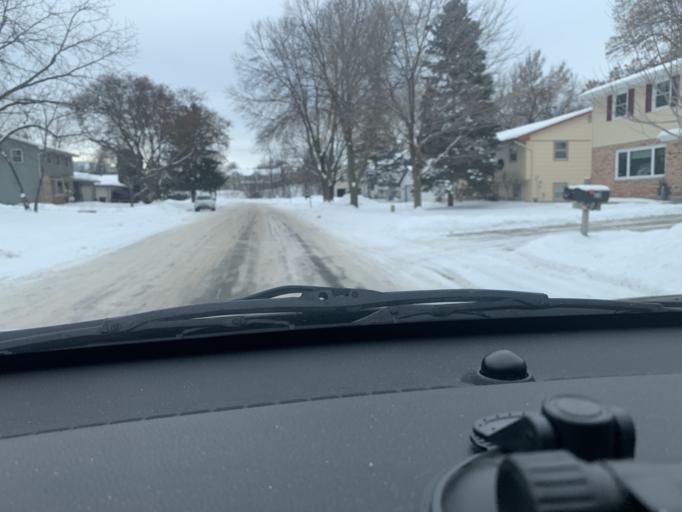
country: US
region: Minnesota
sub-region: Dakota County
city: South Saint Paul
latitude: 44.8848
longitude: -93.0601
